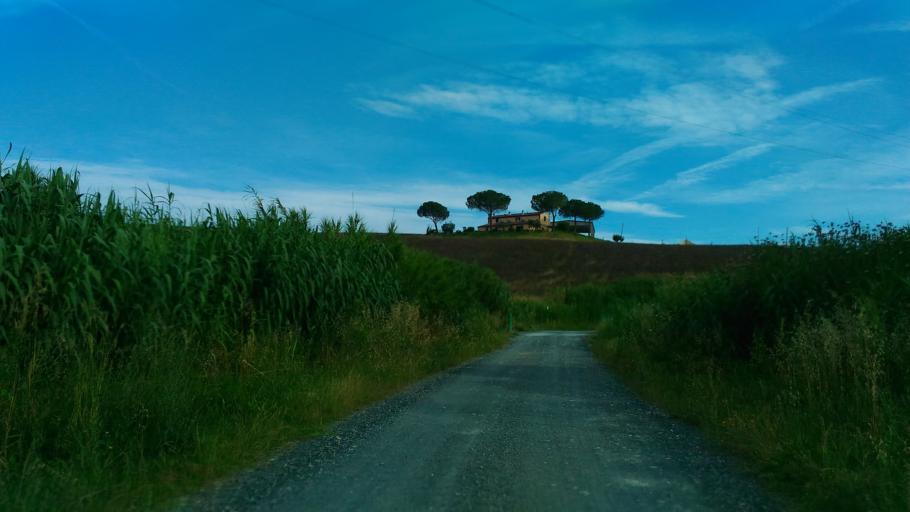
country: IT
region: Tuscany
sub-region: Province of Pisa
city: Santa Luce
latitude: 43.4505
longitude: 10.5230
